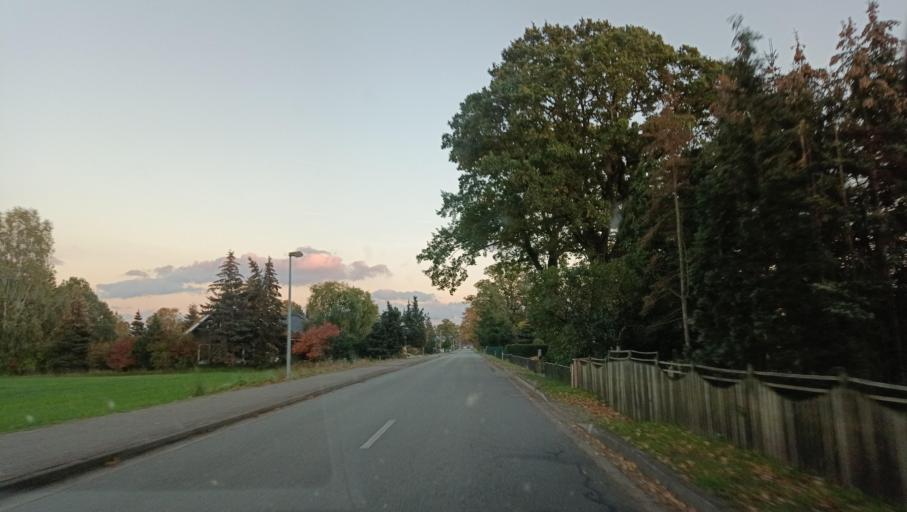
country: DE
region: Mecklenburg-Vorpommern
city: Ludwigslust
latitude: 53.2805
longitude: 11.4904
